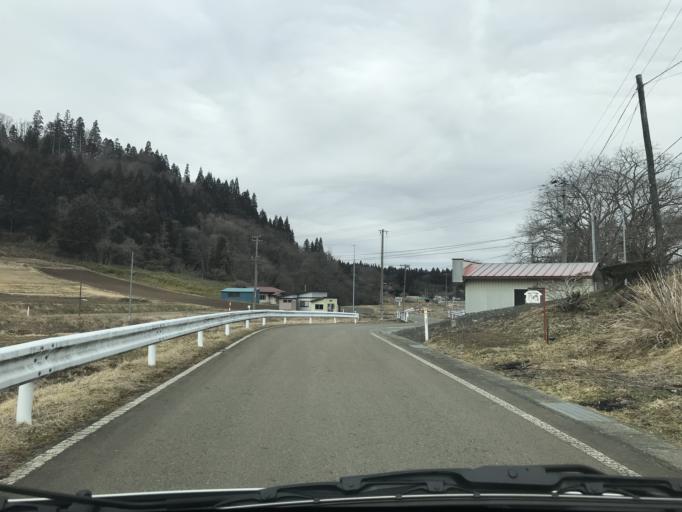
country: JP
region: Iwate
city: Kitakami
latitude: 39.3275
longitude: 141.2344
